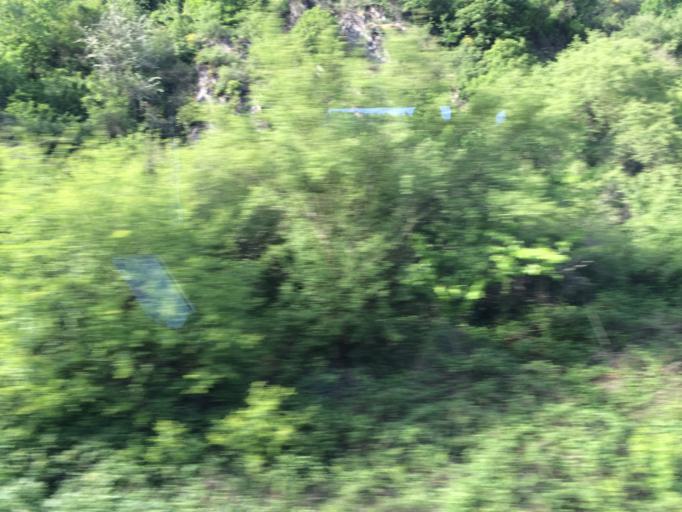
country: DE
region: Rheinland-Pfalz
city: Prath
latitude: 50.1729
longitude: 7.6720
